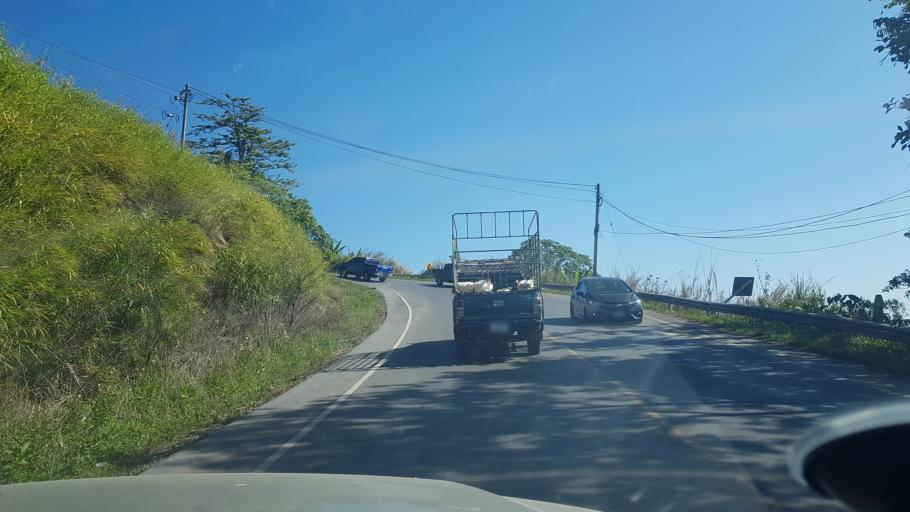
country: TH
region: Phetchabun
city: Lom Kao
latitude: 16.8794
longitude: 101.1022
